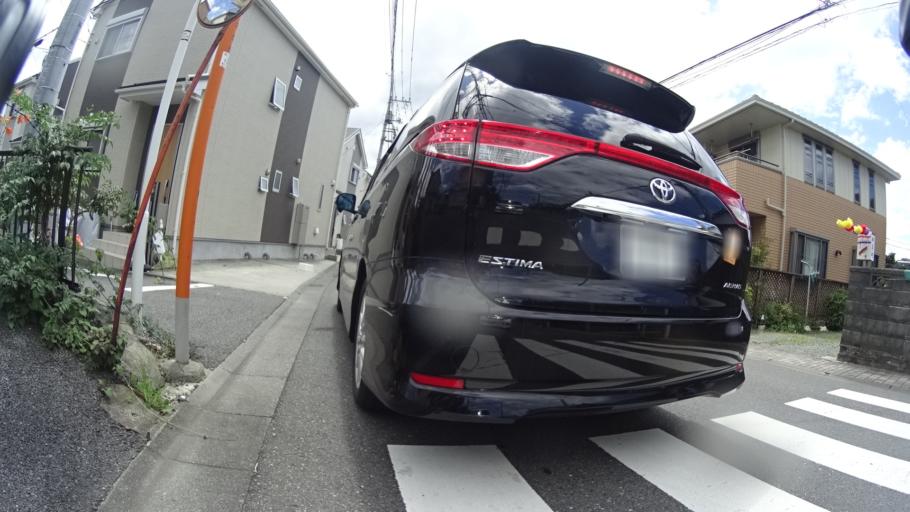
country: JP
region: Tokyo
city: Fussa
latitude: 35.7433
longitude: 139.3220
